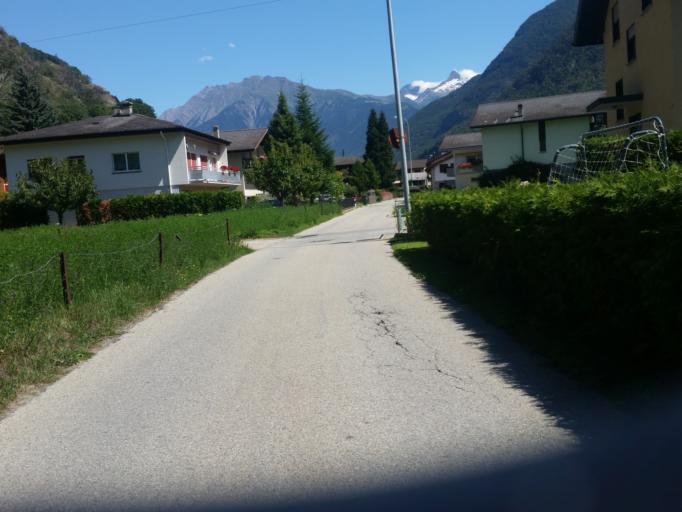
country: CH
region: Valais
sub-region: Visp District
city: Visp
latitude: 46.2996
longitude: 7.9140
